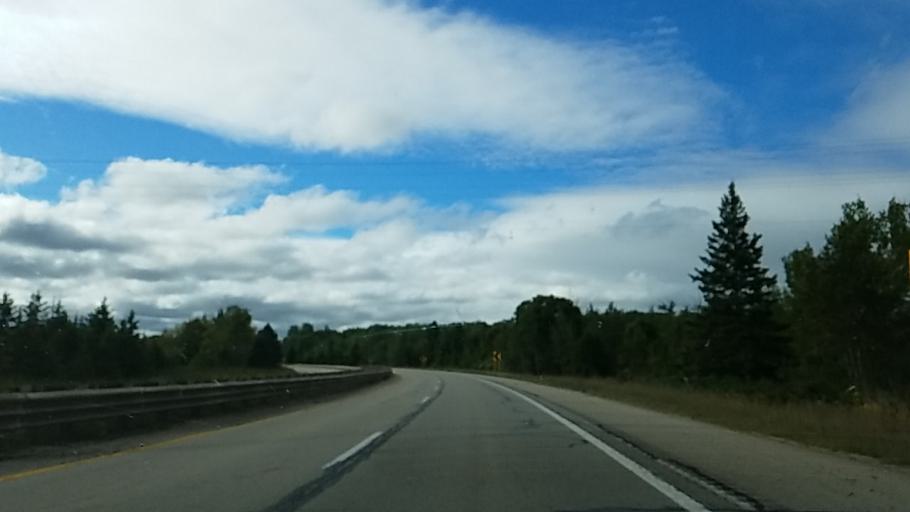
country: US
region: Michigan
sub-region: Mackinac County
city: Saint Ignace
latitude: 45.7676
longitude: -84.7353
